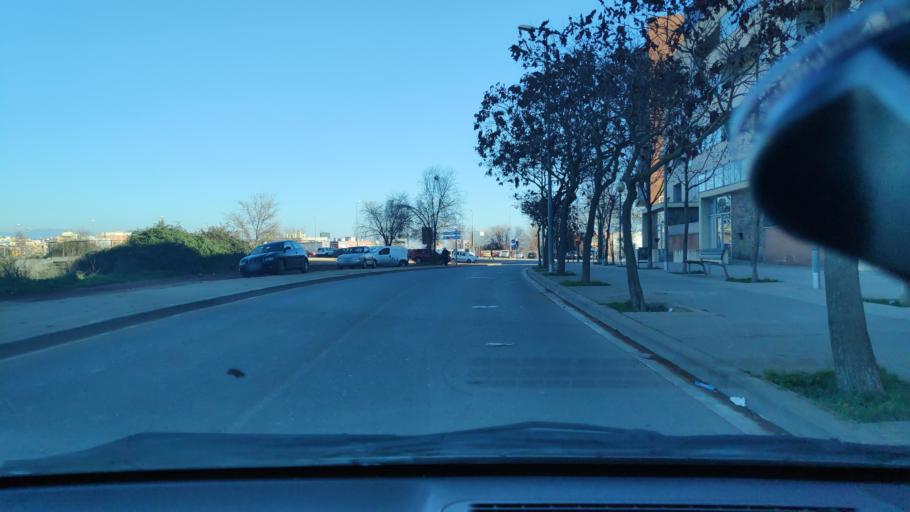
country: ES
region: Catalonia
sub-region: Provincia de Barcelona
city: Sant Quirze del Valles
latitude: 41.5631
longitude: 2.0806
